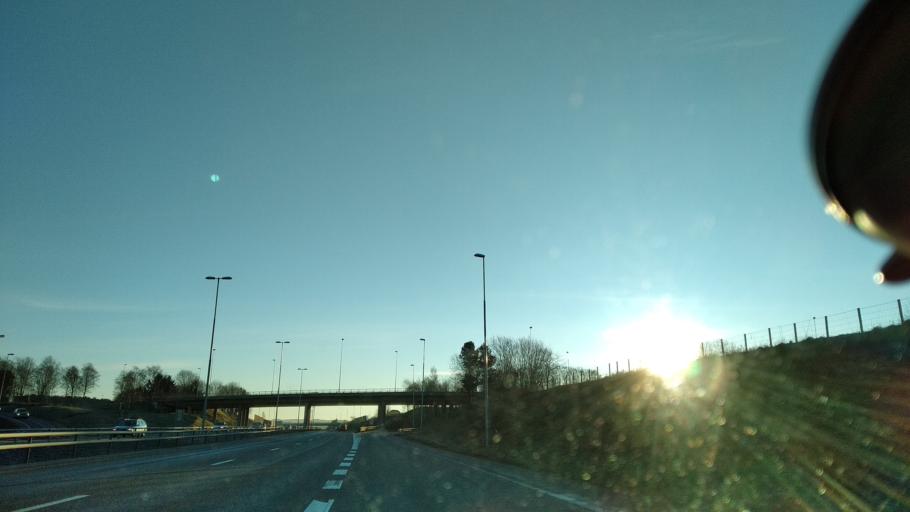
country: NO
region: Rogaland
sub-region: Sandnes
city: Sandnes
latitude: 58.8587
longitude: 5.7113
